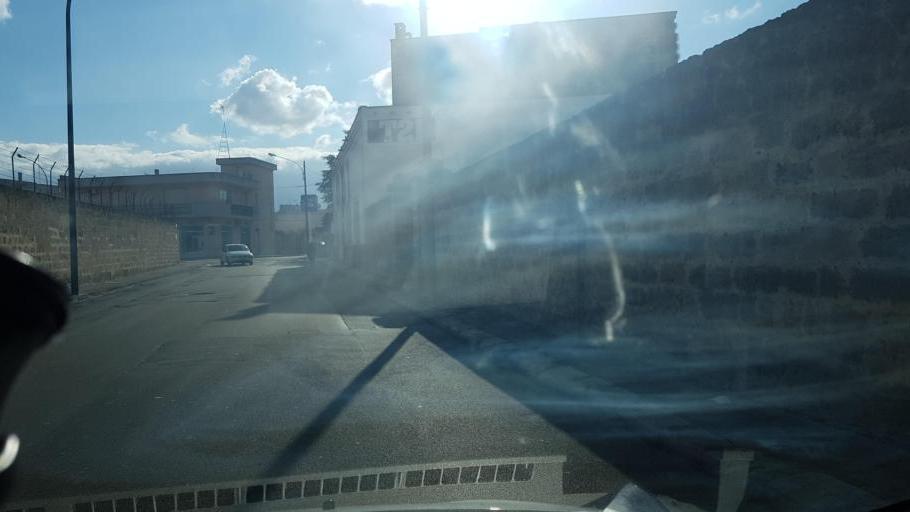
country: IT
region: Apulia
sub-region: Provincia di Lecce
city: Squinzano
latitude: 40.4402
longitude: 18.0375
